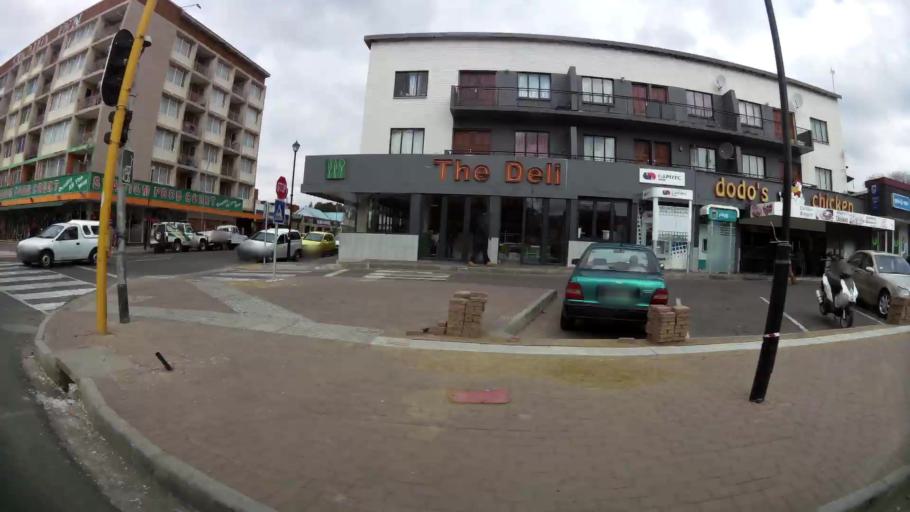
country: ZA
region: Orange Free State
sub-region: Mangaung Metropolitan Municipality
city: Bloemfontein
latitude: -29.1204
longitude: 26.2079
